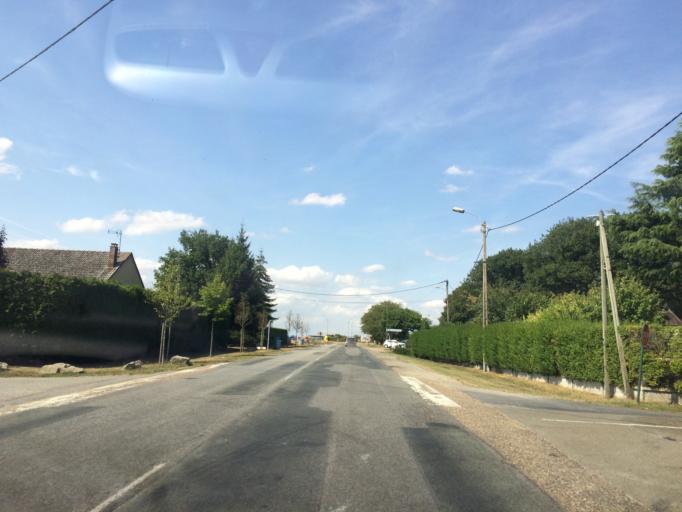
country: FR
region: Haute-Normandie
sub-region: Departement de l'Eure
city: Nonancourt
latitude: 48.7771
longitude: 1.1945
